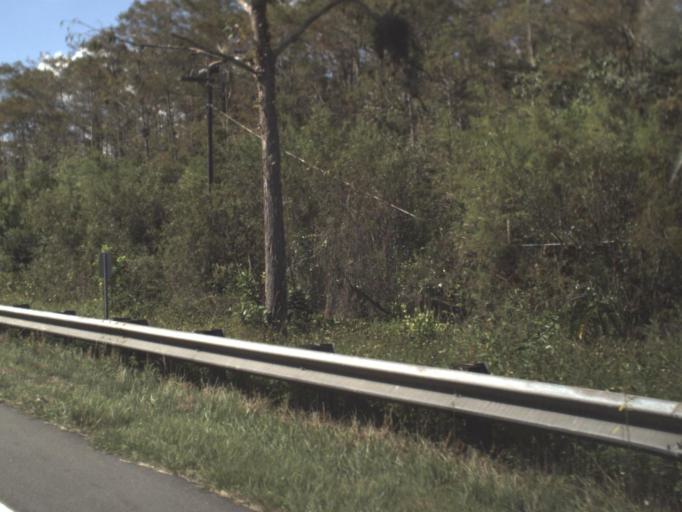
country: US
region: Florida
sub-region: Miami-Dade County
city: Kendall West
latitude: 25.8580
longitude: -81.0443
